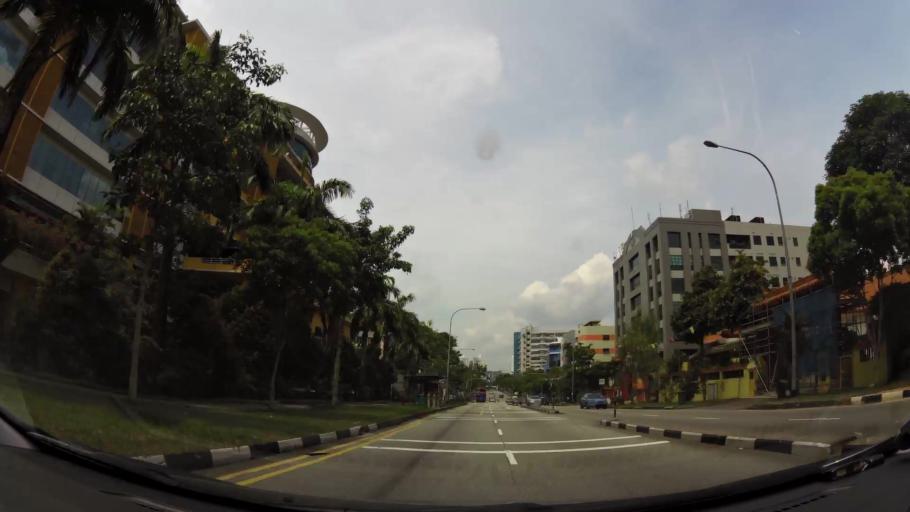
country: SG
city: Singapore
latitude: 1.3396
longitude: 103.7572
